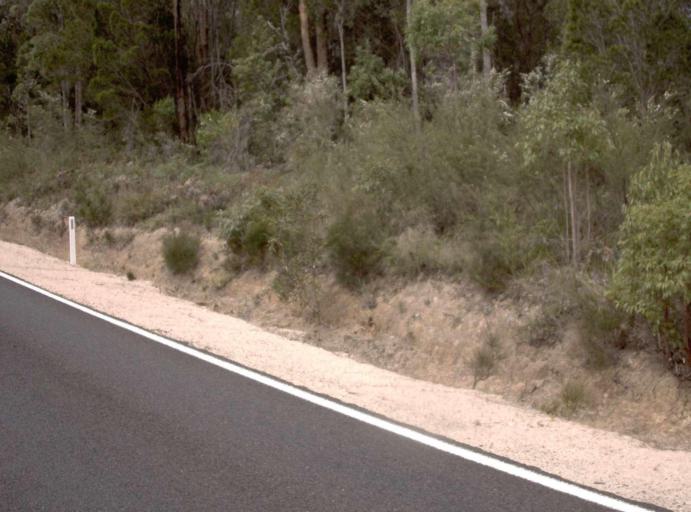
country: AU
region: New South Wales
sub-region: Bega Valley
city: Eden
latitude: -37.4276
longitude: 149.6448
